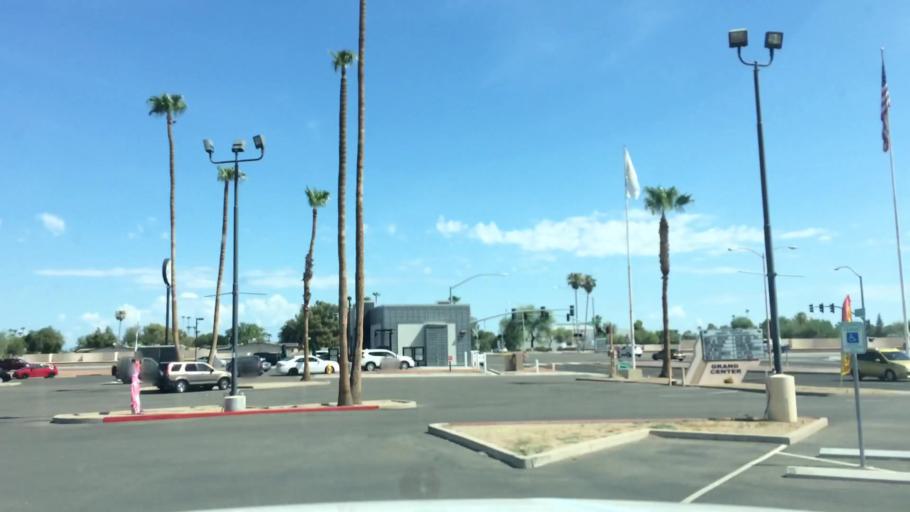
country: US
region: Arizona
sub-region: Maricopa County
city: Youngtown
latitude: 33.6017
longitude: -112.2904
